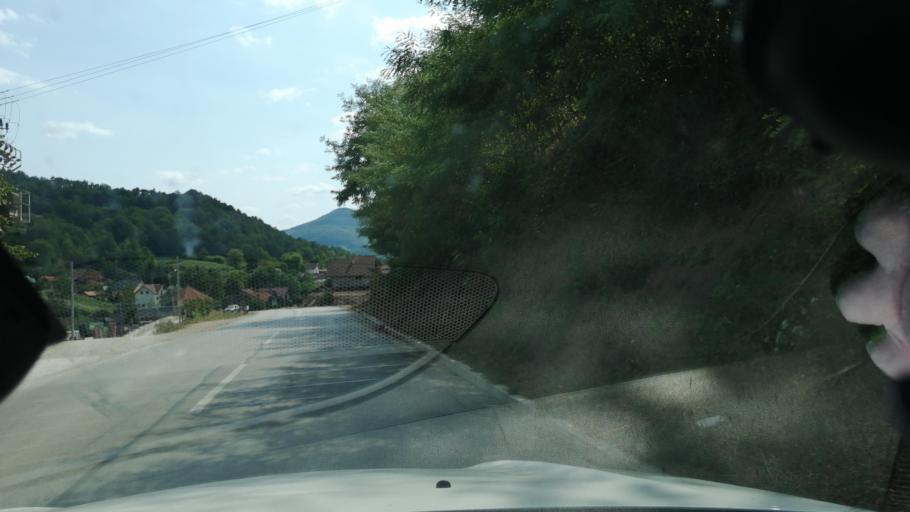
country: RS
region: Central Serbia
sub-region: Moravicki Okrug
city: Ivanjica
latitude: 43.6081
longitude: 20.2347
